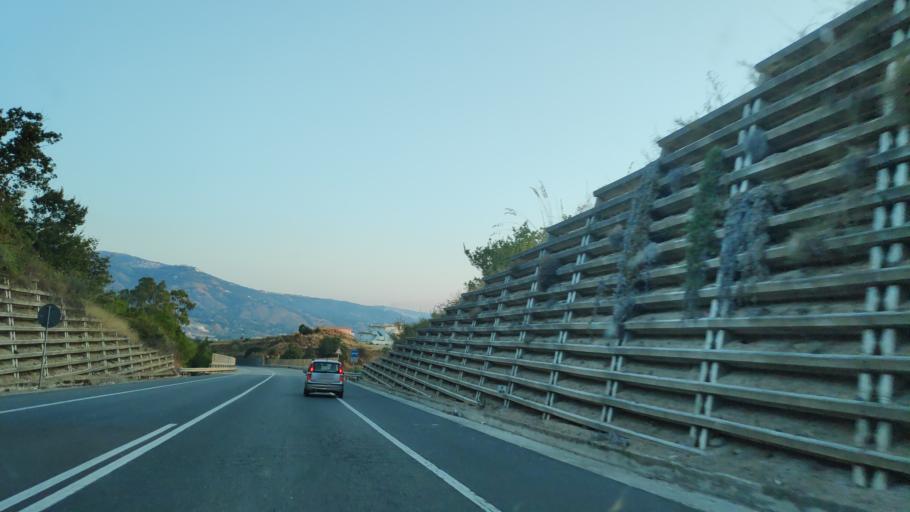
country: IT
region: Calabria
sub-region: Provincia di Catanzaro
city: Soverato Superiore
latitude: 38.6964
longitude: 16.5380
